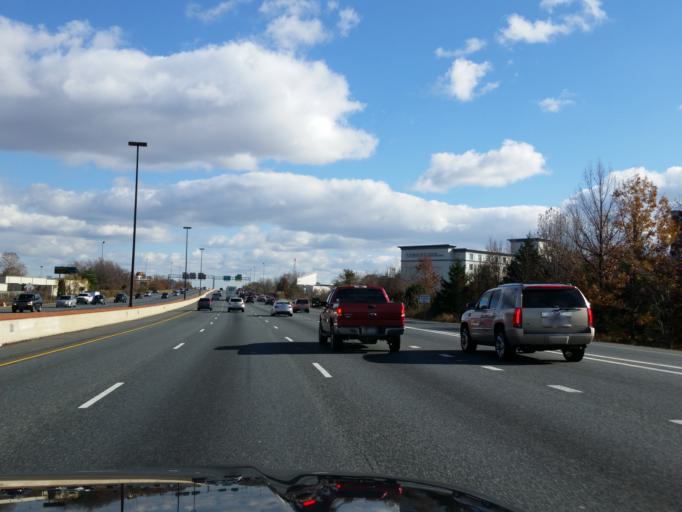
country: US
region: Maryland
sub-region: Anne Arundel County
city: Parole
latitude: 38.9827
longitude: -76.5505
